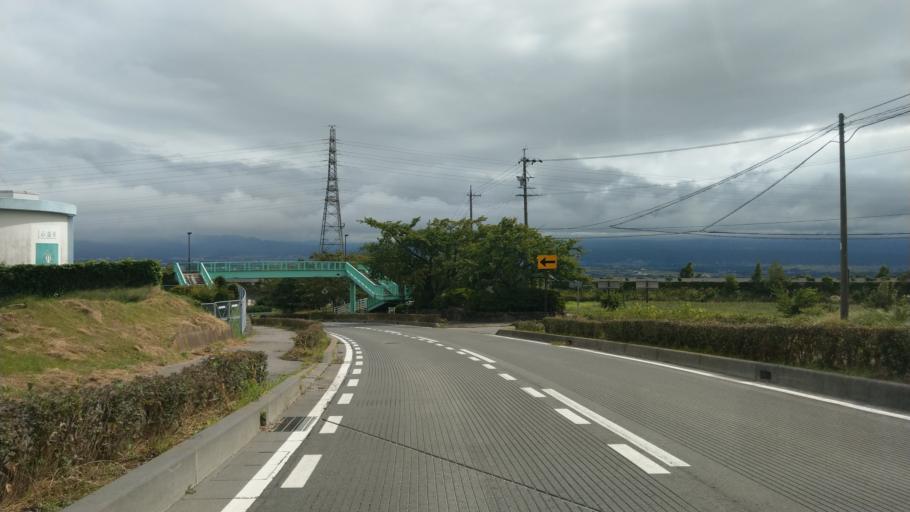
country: JP
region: Nagano
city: Komoro
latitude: 36.3307
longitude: 138.4570
